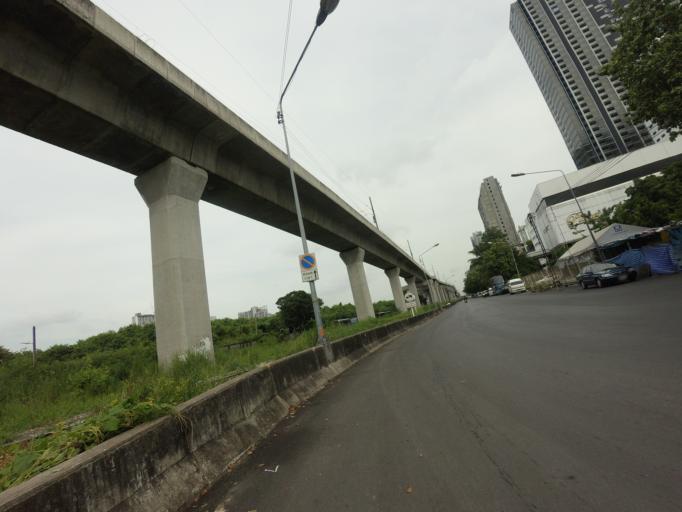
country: TH
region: Bangkok
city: Din Daeng
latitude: 13.7520
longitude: 100.5551
